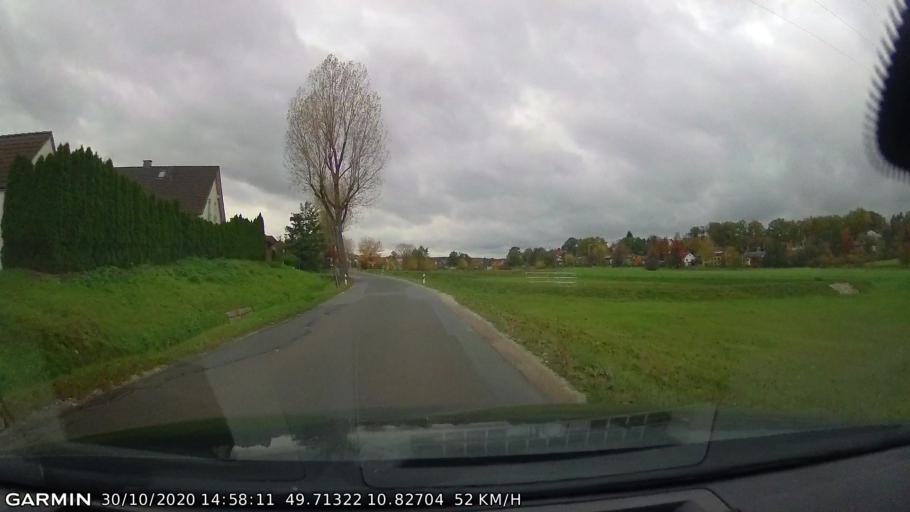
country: DE
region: Bavaria
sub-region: Regierungsbezirk Mittelfranken
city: Hochstadt an der Aisch
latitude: 49.7134
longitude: 10.8265
